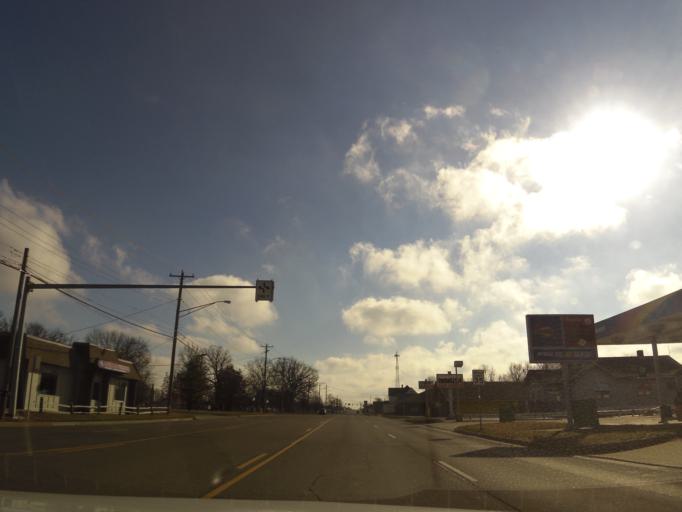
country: US
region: Indiana
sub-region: Jennings County
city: North Vernon
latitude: 39.0115
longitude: -85.6362
